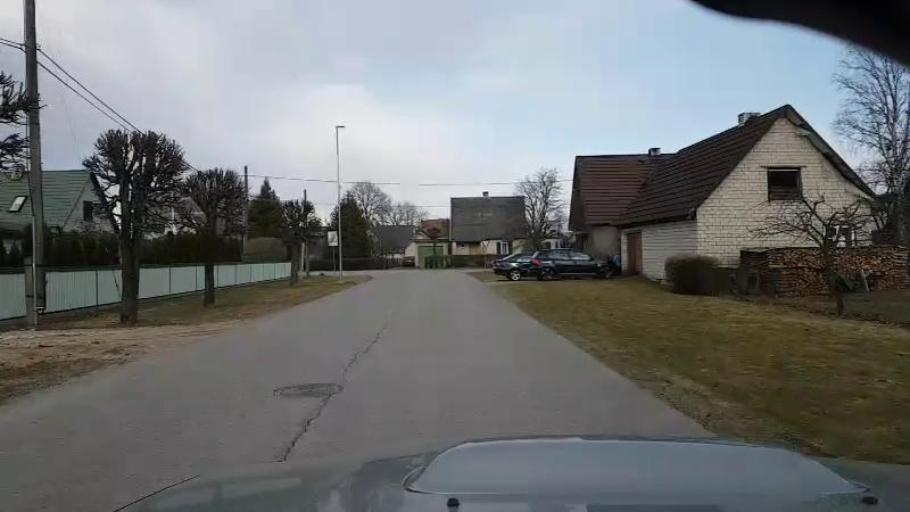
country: EE
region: Jaervamaa
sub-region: Paide linn
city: Paide
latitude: 58.8904
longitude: 25.5567
